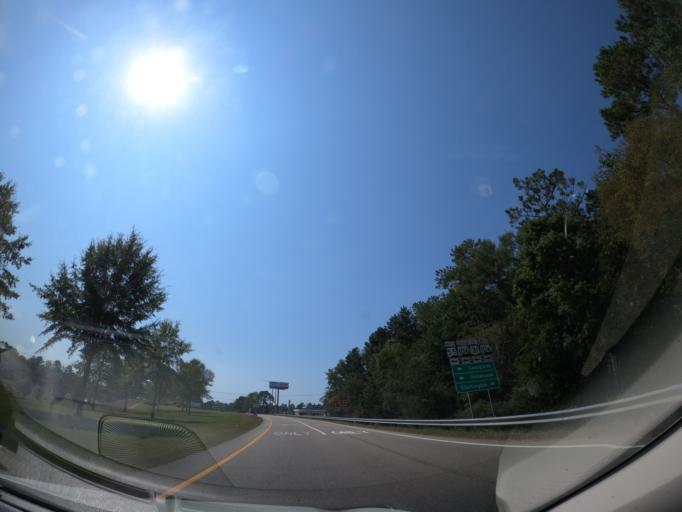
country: US
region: Alabama
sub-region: Butler County
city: Georgiana
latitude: 31.6522
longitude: -86.7750
